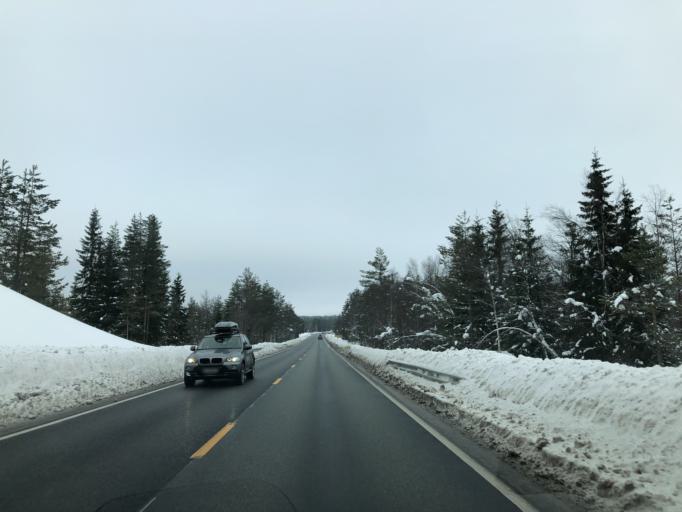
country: NO
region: Hedmark
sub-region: Elverum
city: Elverum
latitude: 60.9936
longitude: 11.7681
